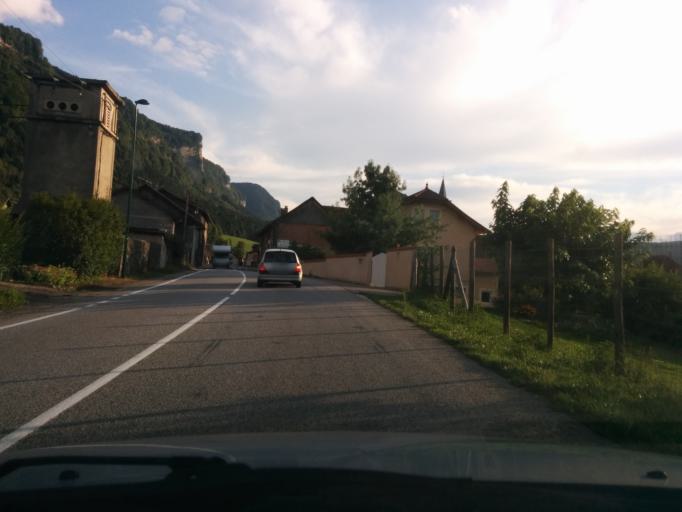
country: FR
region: Rhone-Alpes
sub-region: Departement de l'Isere
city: Saint-Joseph-de-Riviere
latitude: 45.3770
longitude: 5.6980
